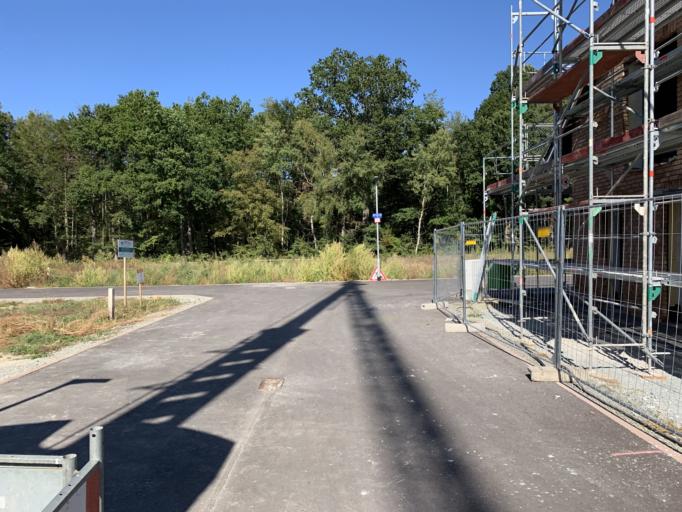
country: DE
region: Hesse
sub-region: Regierungsbezirk Darmstadt
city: Eppertshausen
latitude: 49.9506
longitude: 8.8559
